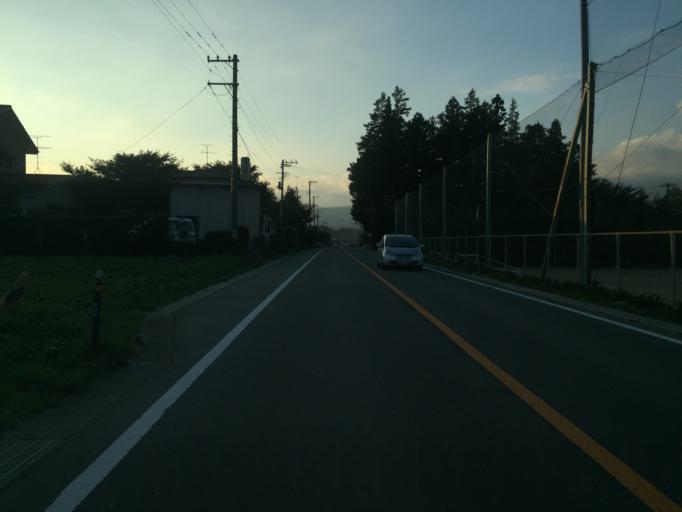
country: JP
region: Fukushima
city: Motomiya
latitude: 37.5436
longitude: 140.3753
